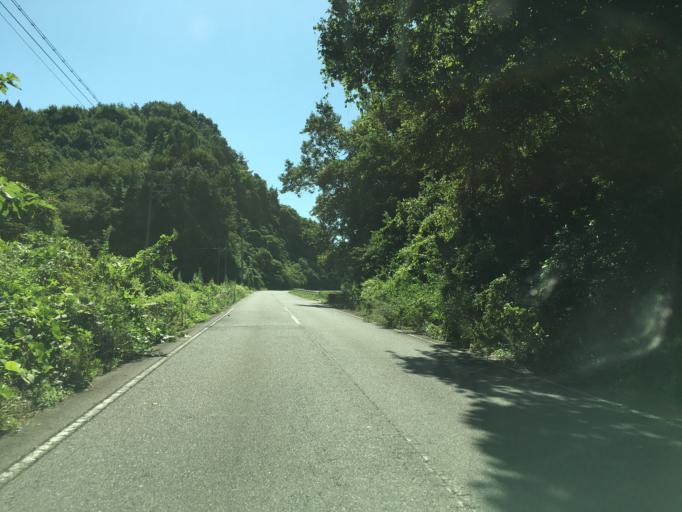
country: JP
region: Fukushima
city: Sukagawa
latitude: 37.2909
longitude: 140.4869
